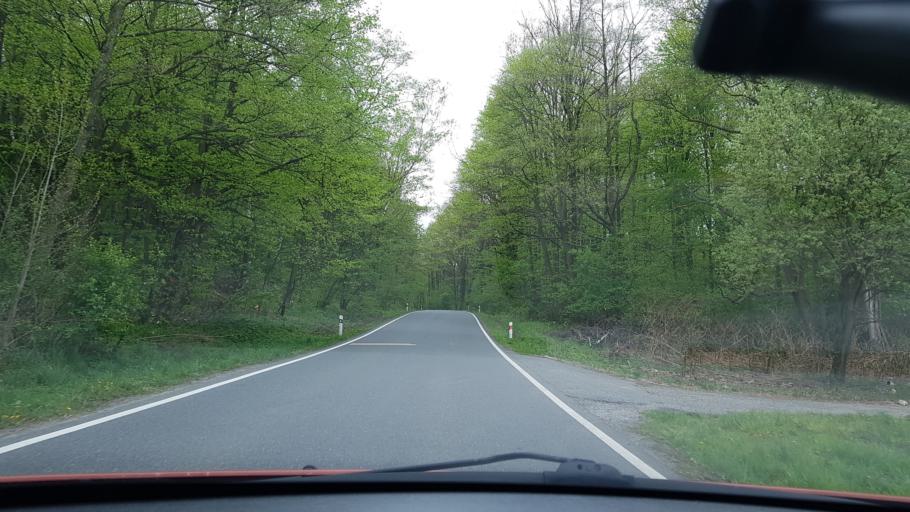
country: CZ
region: Olomoucky
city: Vidnava
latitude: 50.3689
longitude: 17.1928
